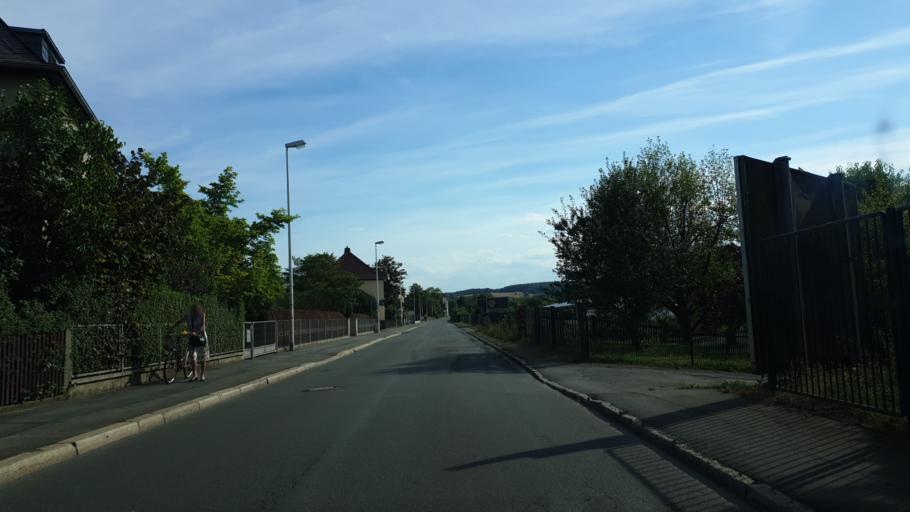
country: DE
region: Thuringia
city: Gera
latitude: 50.8434
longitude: 12.0824
